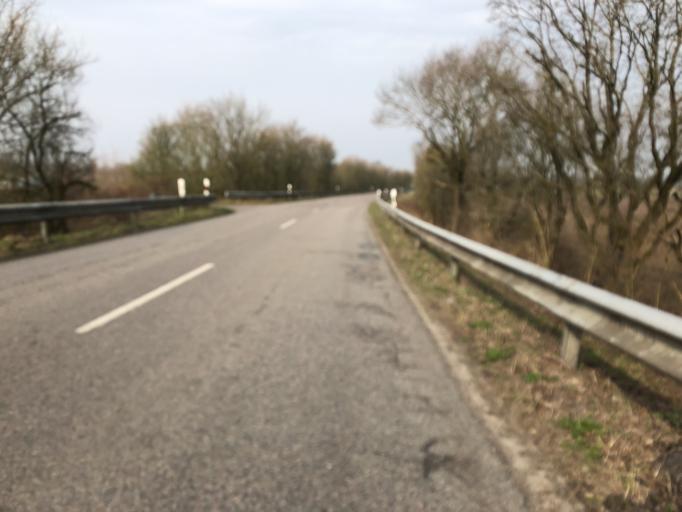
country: DE
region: Schleswig-Holstein
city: Sankelmark
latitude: 54.7022
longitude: 9.3987
